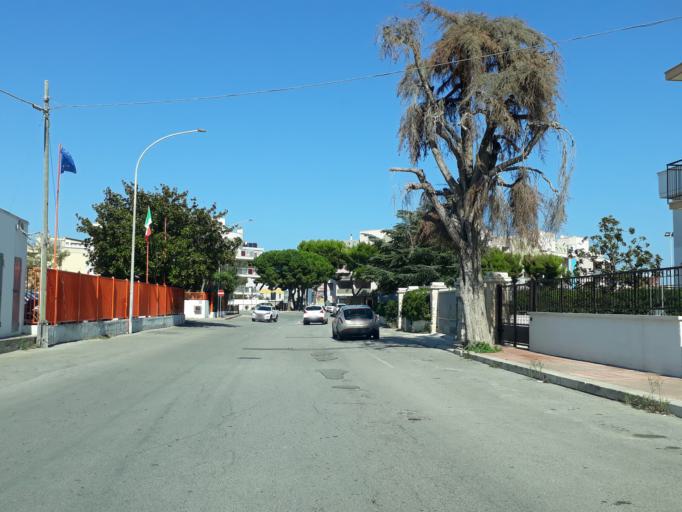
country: IT
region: Apulia
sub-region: Provincia di Bari
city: Monopoli
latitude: 40.9421
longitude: 17.3035
